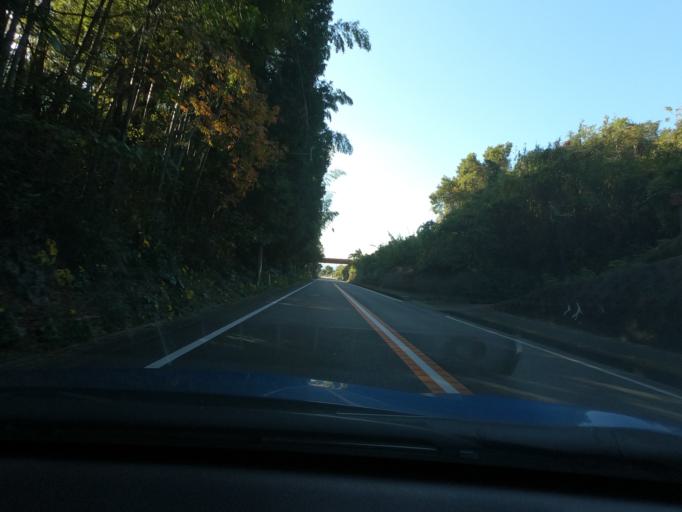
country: JP
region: Kumamoto
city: Minamata
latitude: 32.1622
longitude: 130.3719
